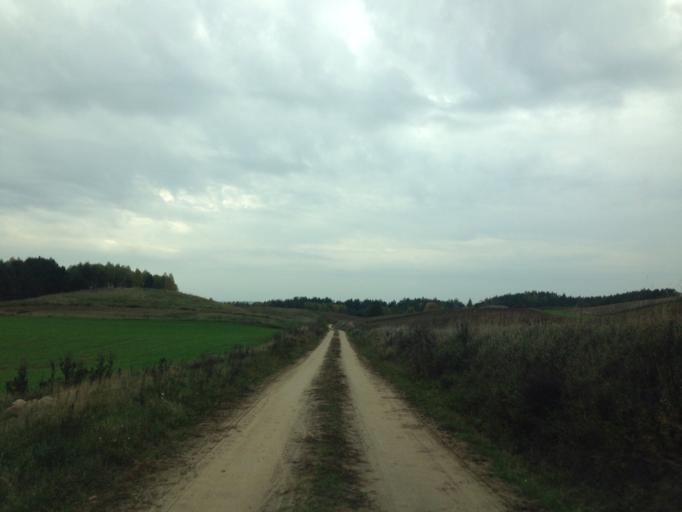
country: PL
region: Kujawsko-Pomorskie
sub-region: Powiat brodnicki
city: Bartniczka
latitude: 53.2778
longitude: 19.6824
